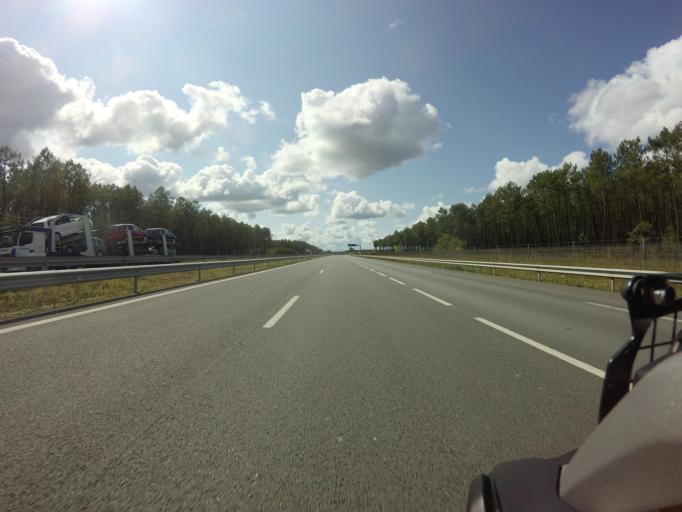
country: FR
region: Aquitaine
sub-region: Departement des Landes
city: Magescq
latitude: 43.8098
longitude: -1.1976
